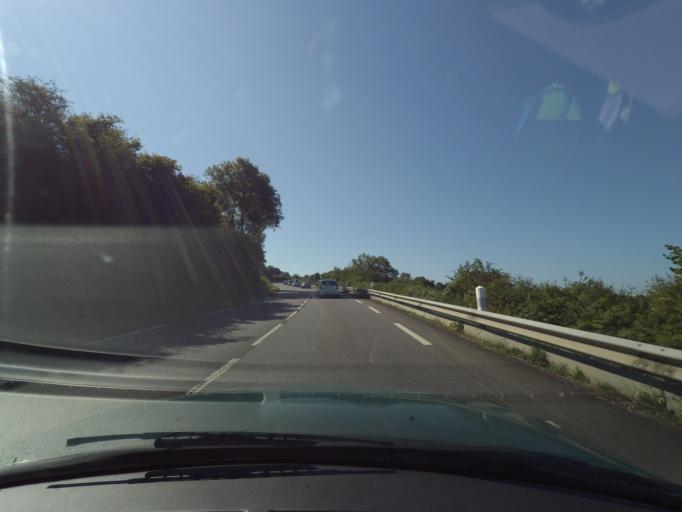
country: FR
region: Limousin
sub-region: Departement de la Haute-Vienne
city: Peyrat-de-Bellac
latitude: 46.1613
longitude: 0.9596
